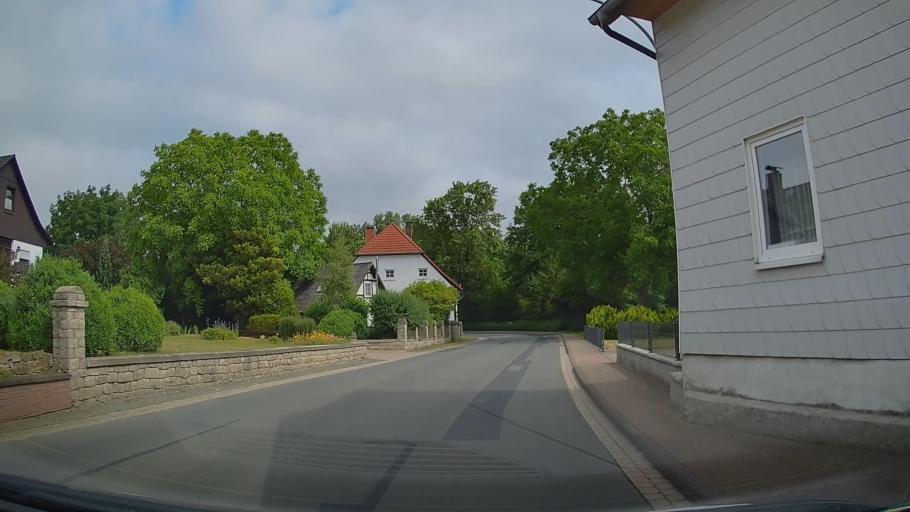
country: DE
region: Lower Saxony
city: Aerzen
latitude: 52.0410
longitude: 9.1981
